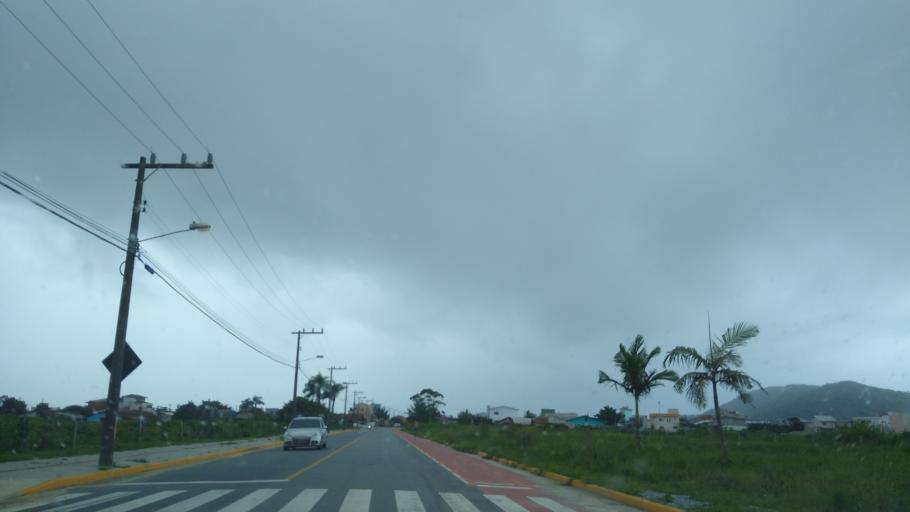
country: BR
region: Santa Catarina
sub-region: Sao Francisco Do Sul
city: Sao Francisco do Sul
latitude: -26.2367
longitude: -48.5116
